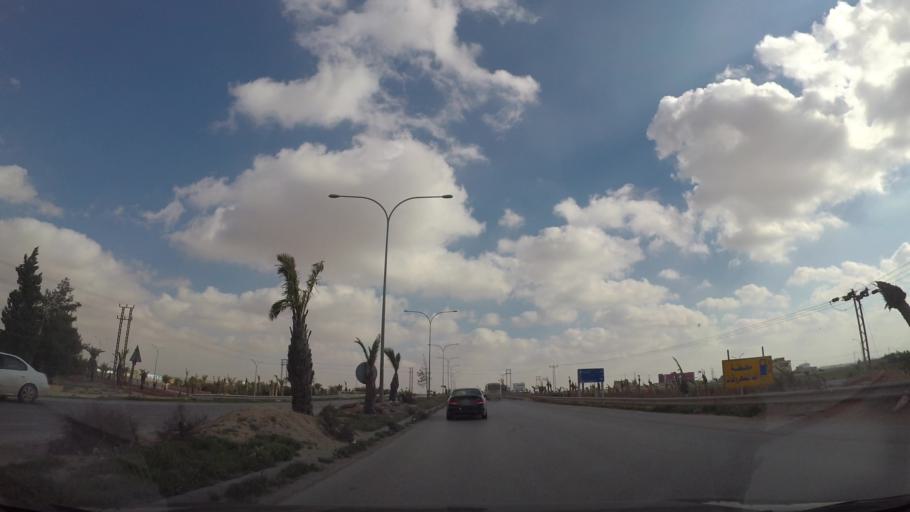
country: JO
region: Amman
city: Al Jizah
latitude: 31.6958
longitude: 35.9551
